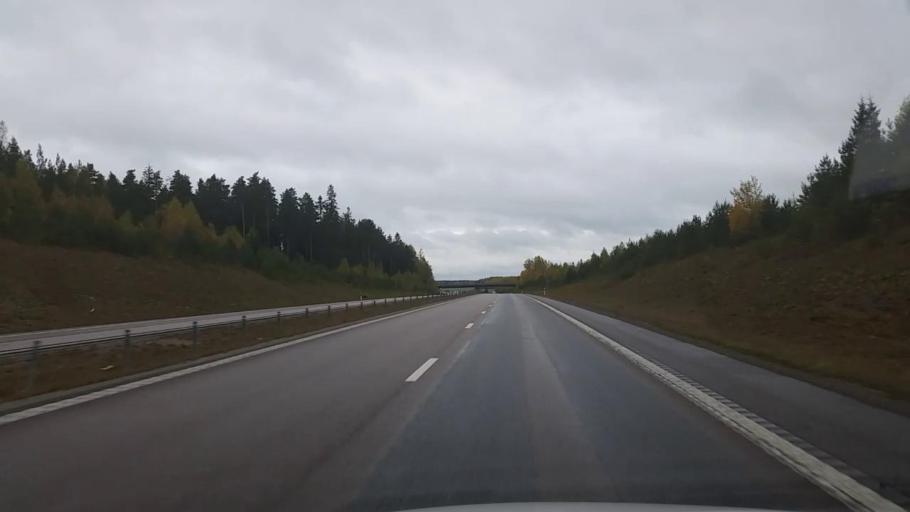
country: SE
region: Uppsala
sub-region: Osthammars Kommun
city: Bjorklinge
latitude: 60.1339
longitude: 17.5474
